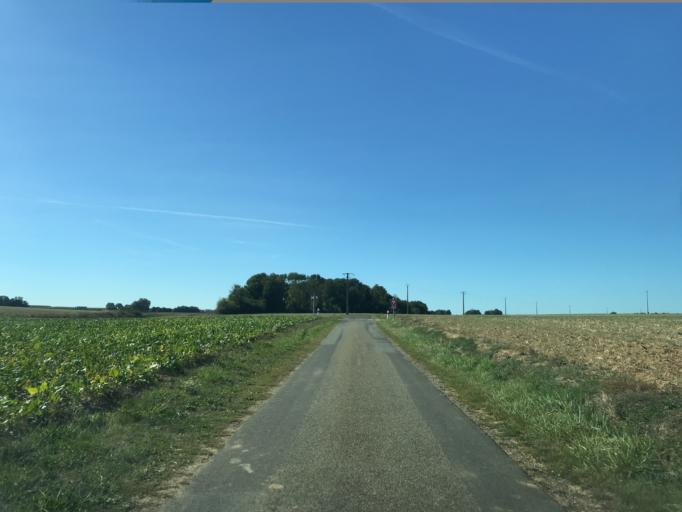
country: FR
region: Haute-Normandie
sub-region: Departement de l'Eure
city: Ande
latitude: 49.1749
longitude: 1.2597
